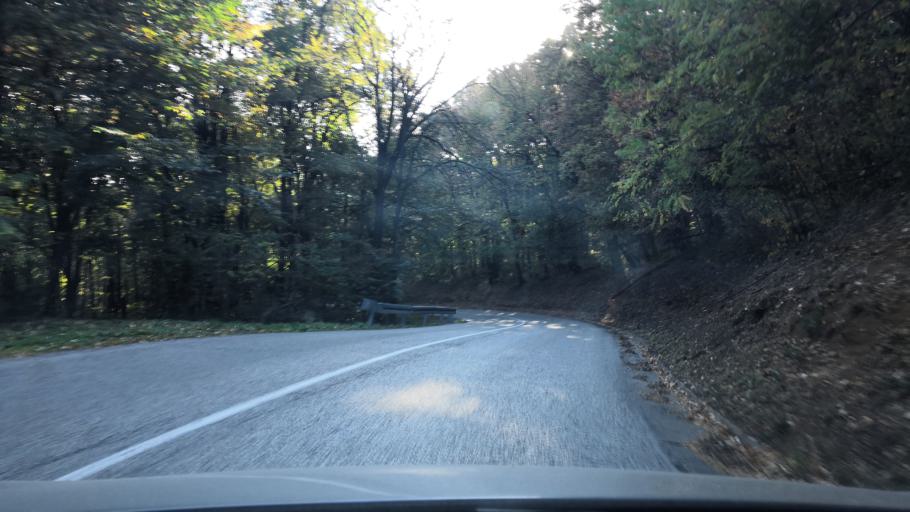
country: RS
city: Vrdnik
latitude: 45.1558
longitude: 19.7756
